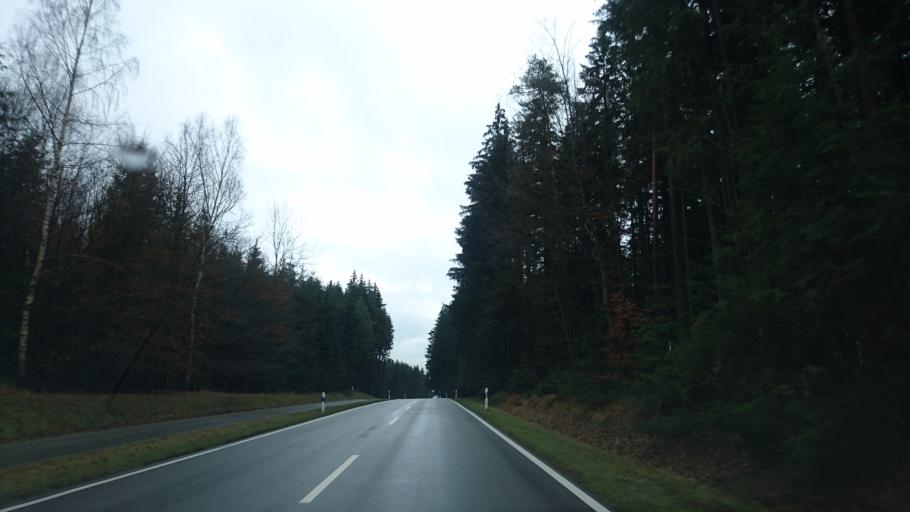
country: DE
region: Bavaria
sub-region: Swabia
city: Bonstetten
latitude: 48.4657
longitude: 10.6959
